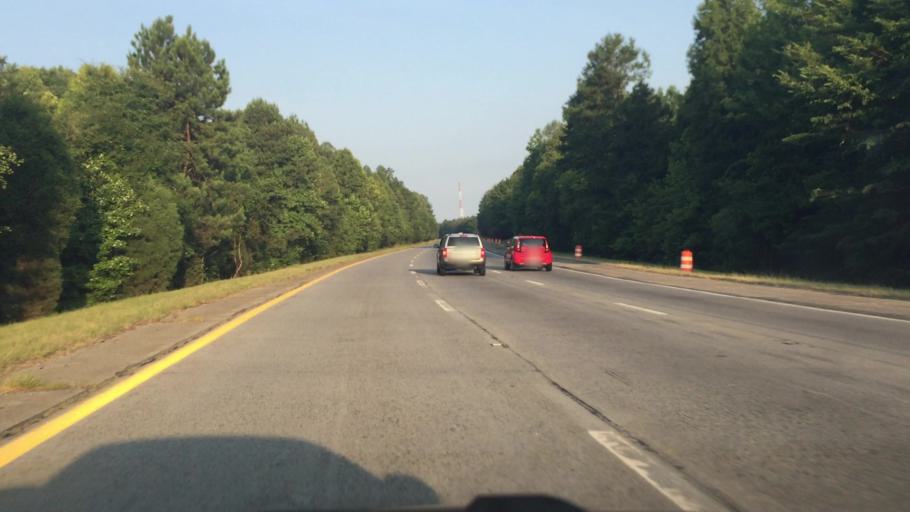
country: US
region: North Carolina
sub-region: Davidson County
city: Thomasville
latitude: 35.8281
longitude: -80.1544
